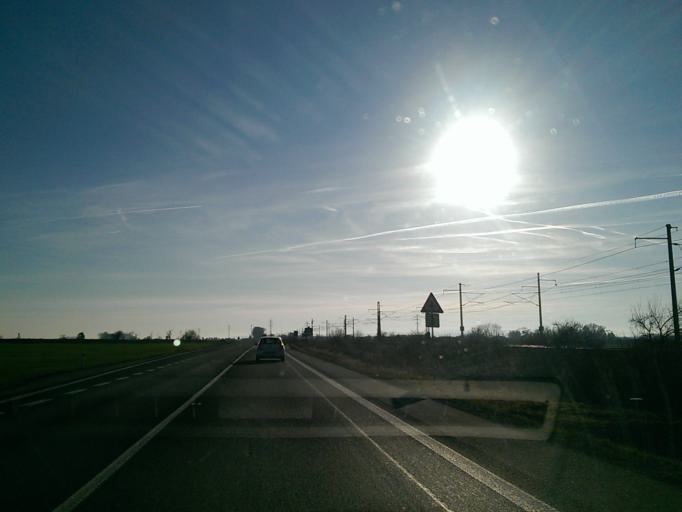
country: CZ
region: Olomoucky
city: Horni Mostenice
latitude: 49.3948
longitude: 17.4538
